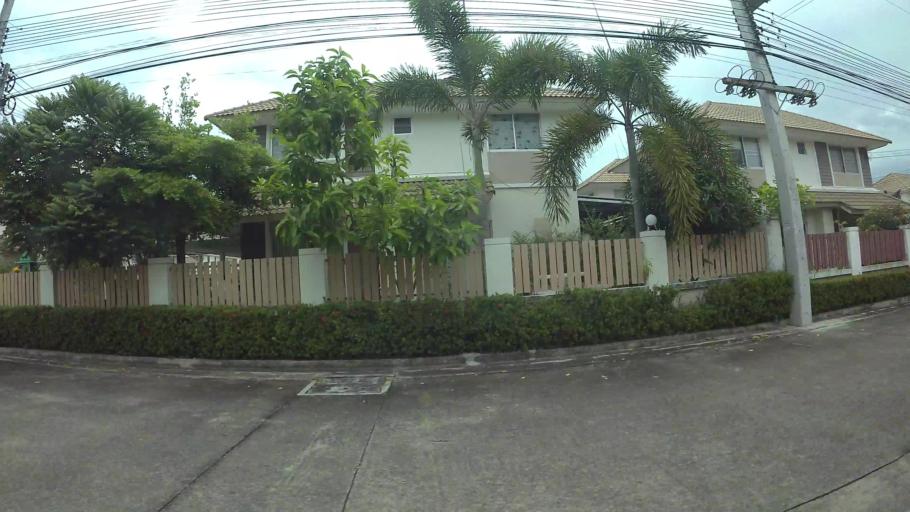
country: TH
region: Chon Buri
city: Si Racha
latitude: 13.1433
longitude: 100.9797
